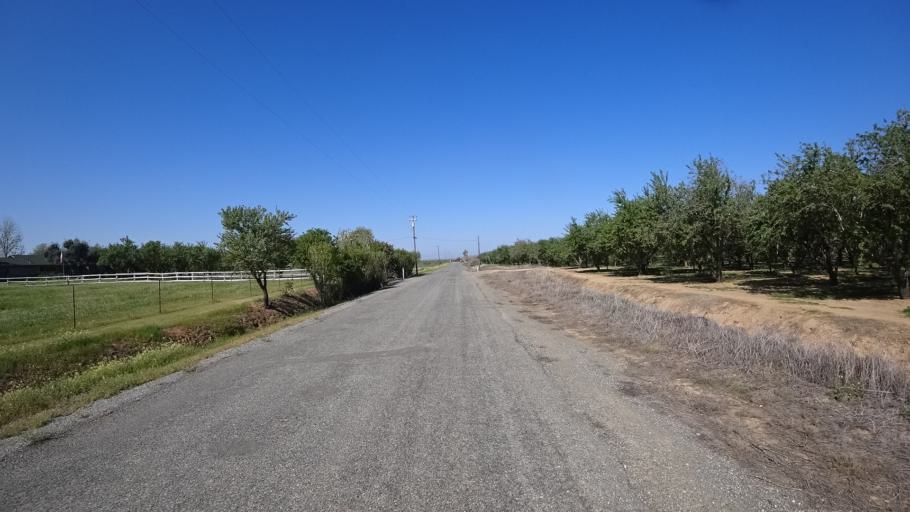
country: US
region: California
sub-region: Glenn County
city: Hamilton City
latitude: 39.6451
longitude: -122.0144
